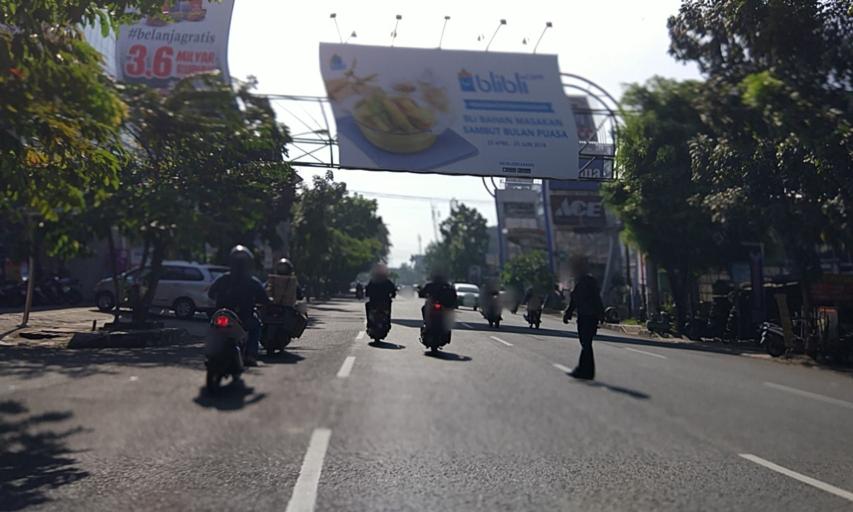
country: ID
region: West Java
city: Bandung
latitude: -6.9146
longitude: 107.6321
